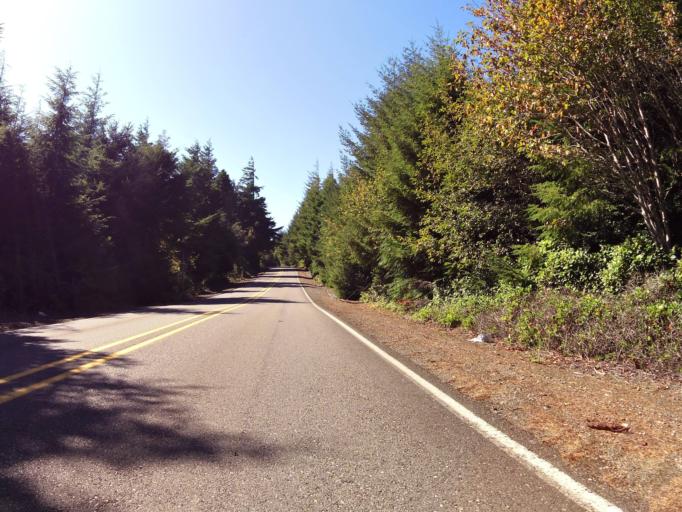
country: US
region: Oregon
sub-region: Coos County
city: Barview
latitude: 43.2418
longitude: -124.3349
